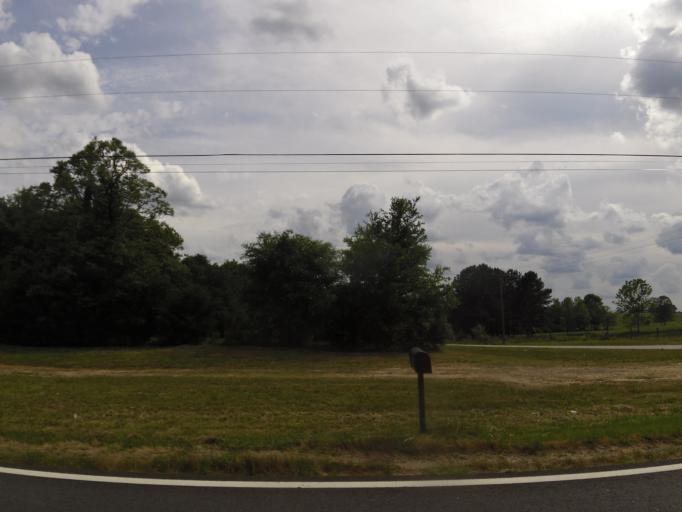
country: US
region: Georgia
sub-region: McDuffie County
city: Thomson
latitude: 33.5263
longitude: -82.4721
